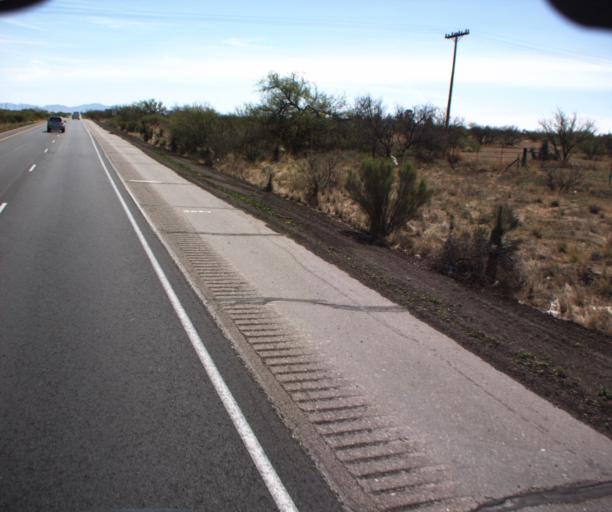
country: US
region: Arizona
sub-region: Cochise County
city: Mescal
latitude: 31.9628
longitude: -110.4255
